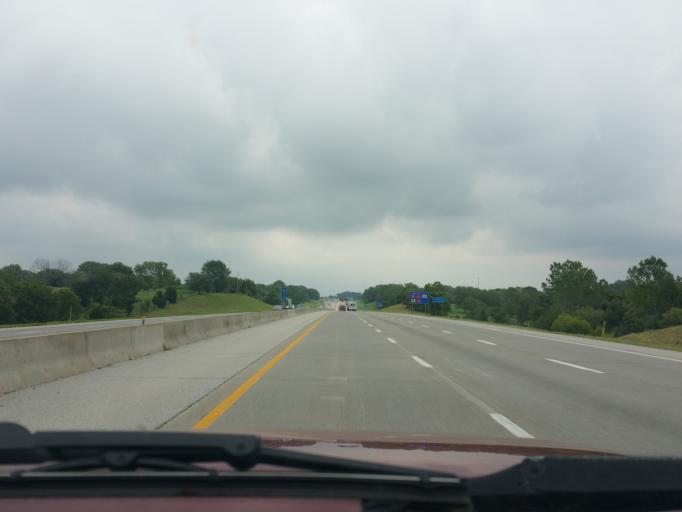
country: US
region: Kansas
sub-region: Wyandotte County
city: Edwardsville
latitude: 39.1048
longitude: -94.7786
